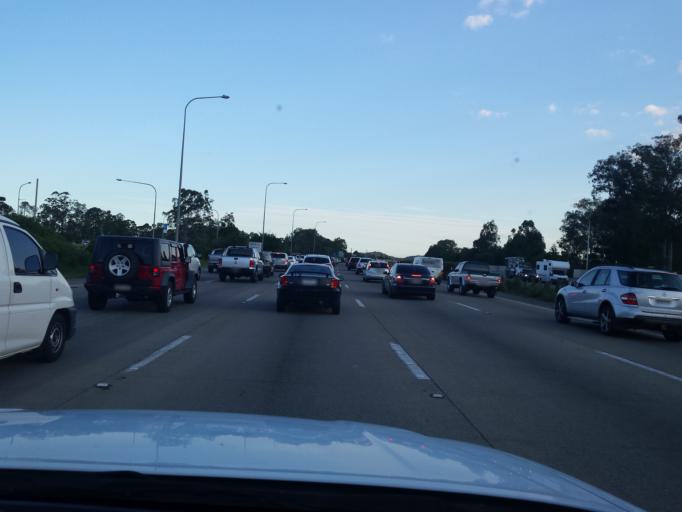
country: AU
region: Queensland
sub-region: Gold Coast
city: Oxenford
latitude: -27.8657
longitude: 153.3125
